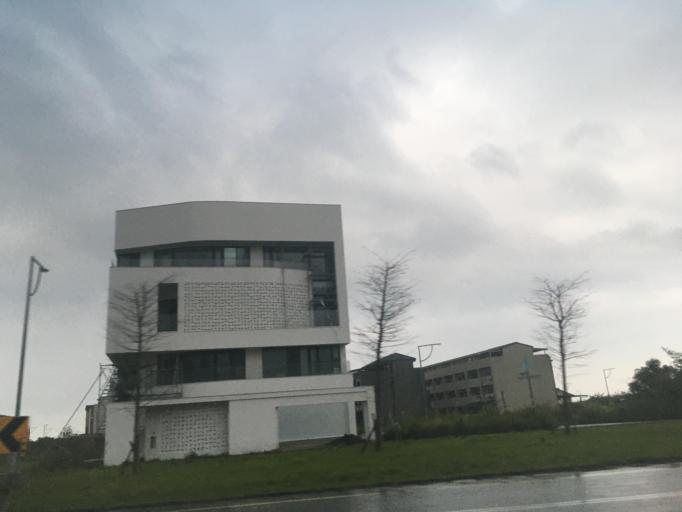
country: TW
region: Taiwan
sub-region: Yilan
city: Yilan
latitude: 24.8642
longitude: 121.8288
